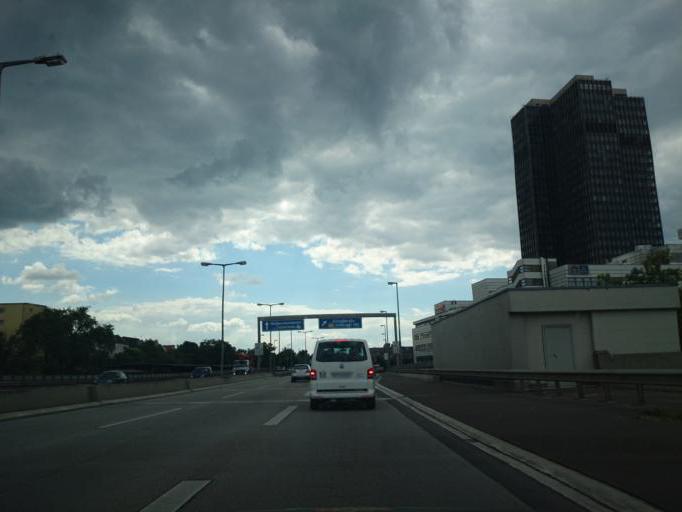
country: DE
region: Berlin
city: Steglitz Bezirk
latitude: 52.4569
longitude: 13.3235
